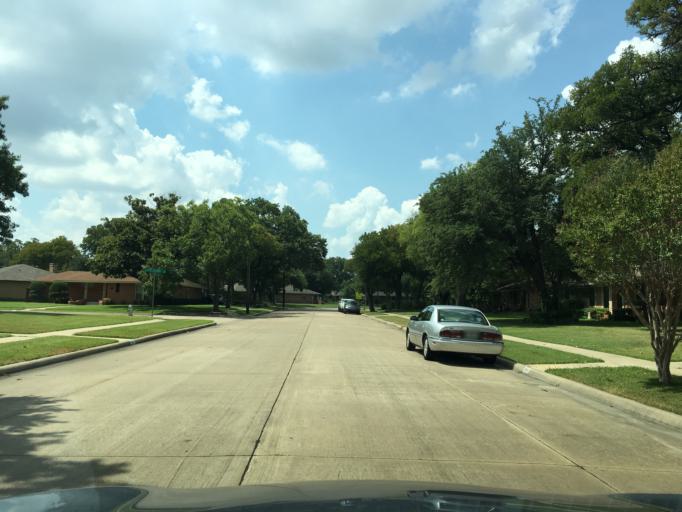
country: US
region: Texas
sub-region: Dallas County
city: Garland
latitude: 32.9361
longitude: -96.6428
